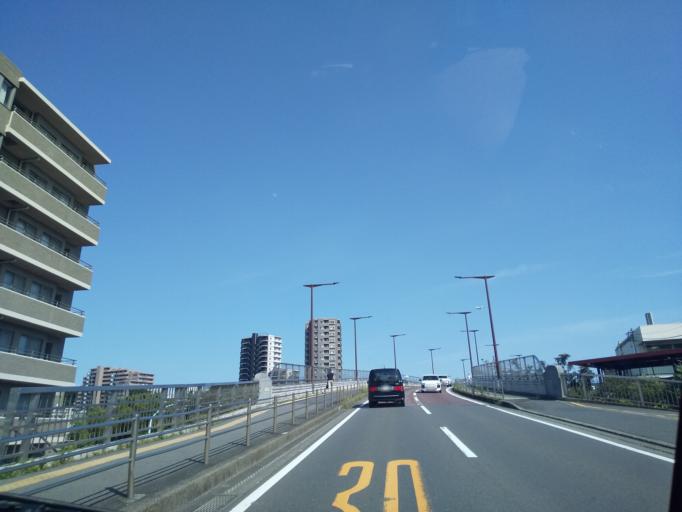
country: JP
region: Kanagawa
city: Zama
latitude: 35.4679
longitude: 139.4138
